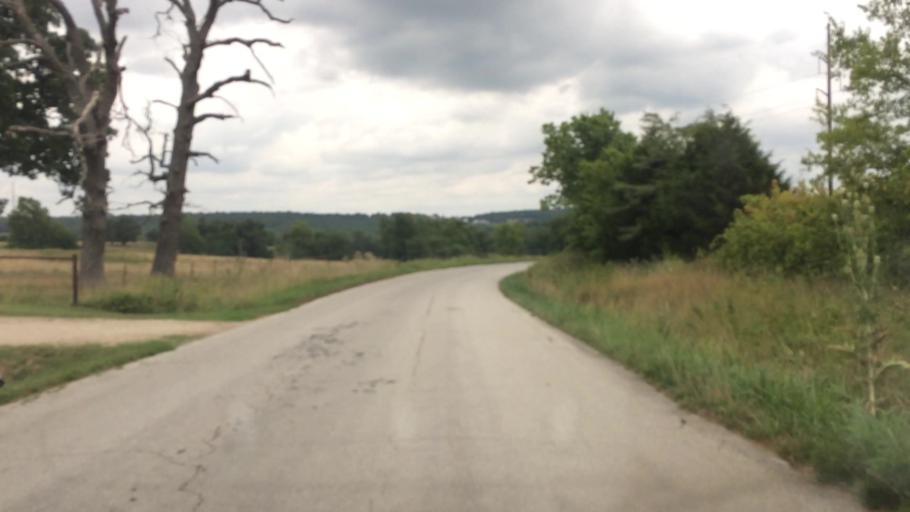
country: US
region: Missouri
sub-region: Greene County
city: Strafford
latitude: 37.3190
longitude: -93.0635
